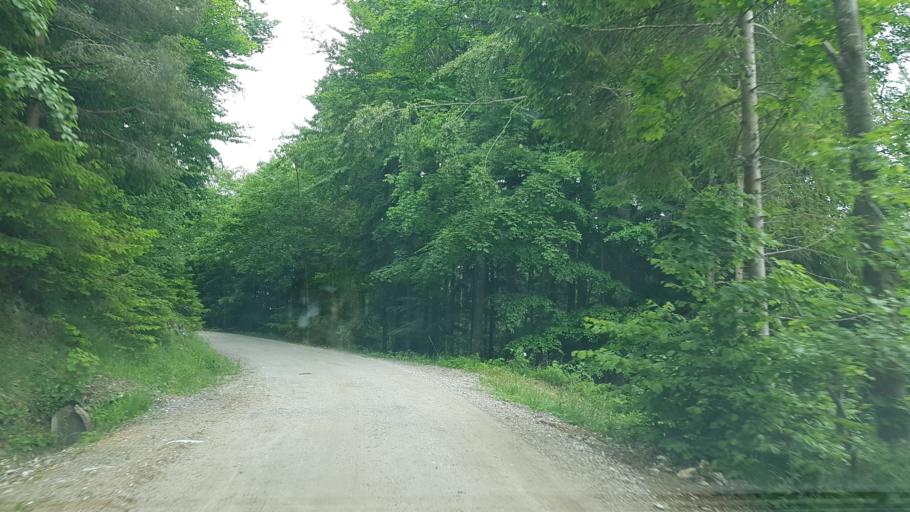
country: SI
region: Dobrna
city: Dobrna
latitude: 46.3792
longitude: 15.2428
